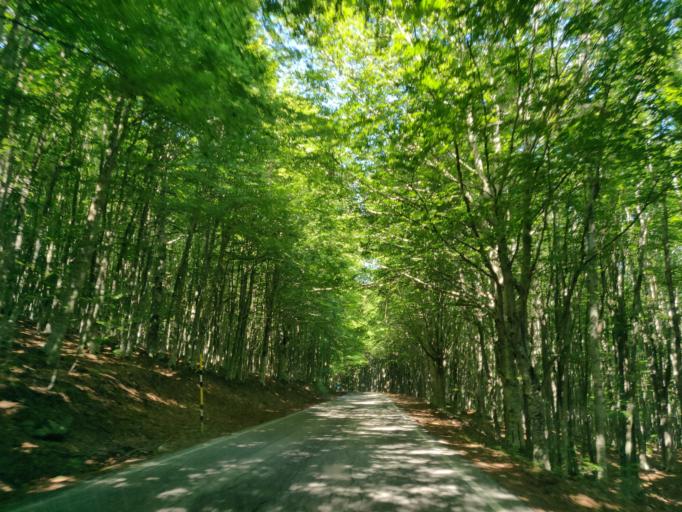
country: IT
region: Tuscany
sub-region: Provincia di Siena
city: Abbadia San Salvatore
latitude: 42.9029
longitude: 11.6233
